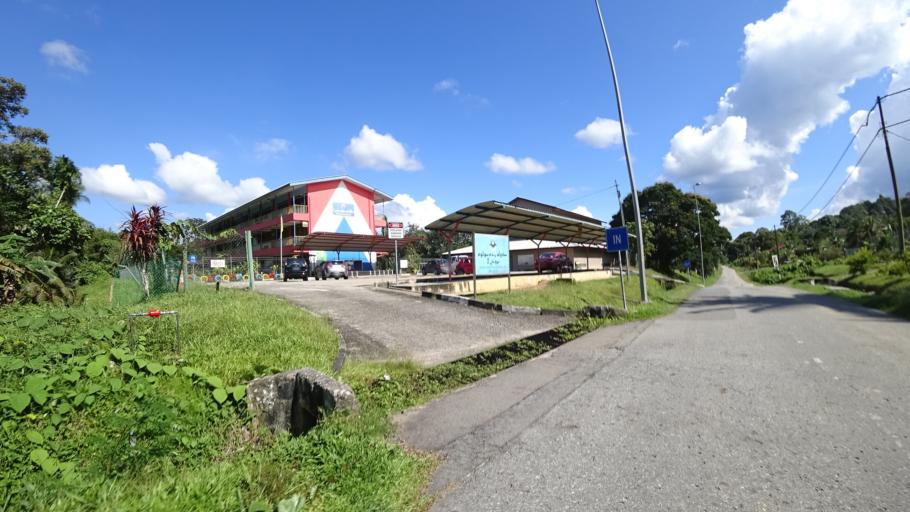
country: BN
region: Tutong
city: Tutong
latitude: 4.7431
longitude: 114.7883
